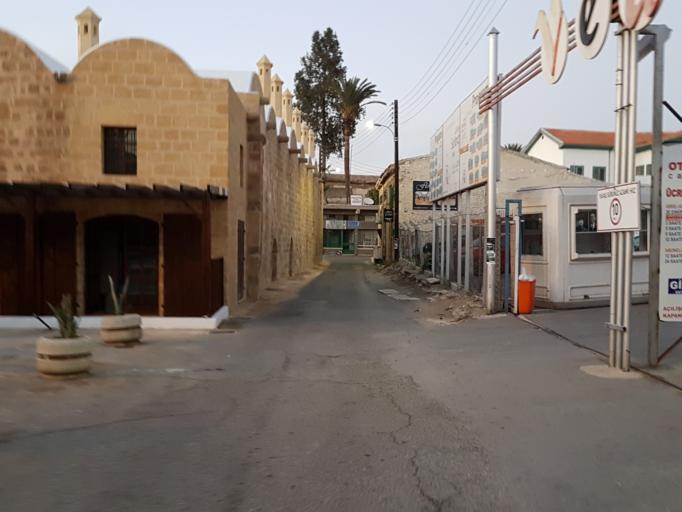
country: CY
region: Lefkosia
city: Nicosia
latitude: 35.1768
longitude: 33.3627
